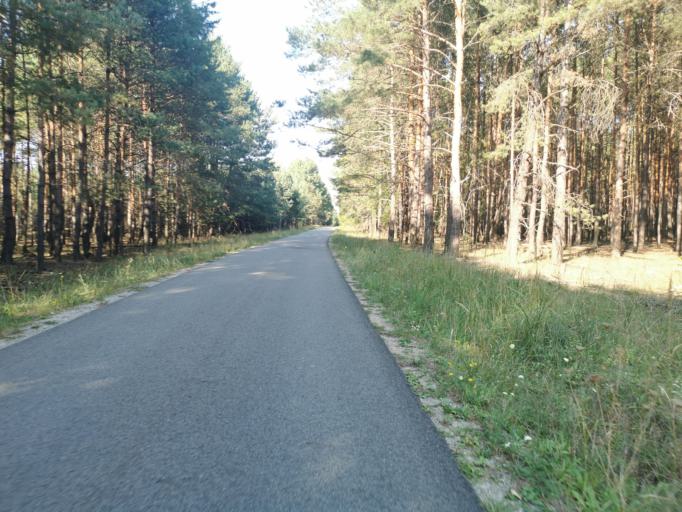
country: SK
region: Trnavsky
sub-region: Okres Senica
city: Senica
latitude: 48.6354
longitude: 17.2609
